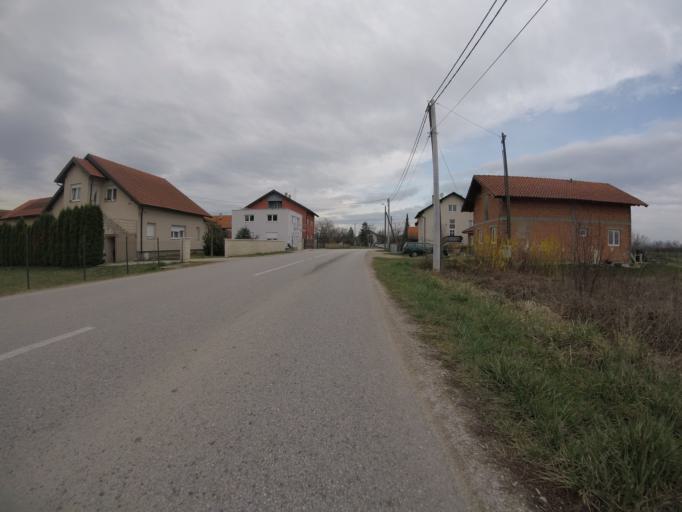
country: HR
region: Zagrebacka
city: Gradici
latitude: 45.7130
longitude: 16.0271
